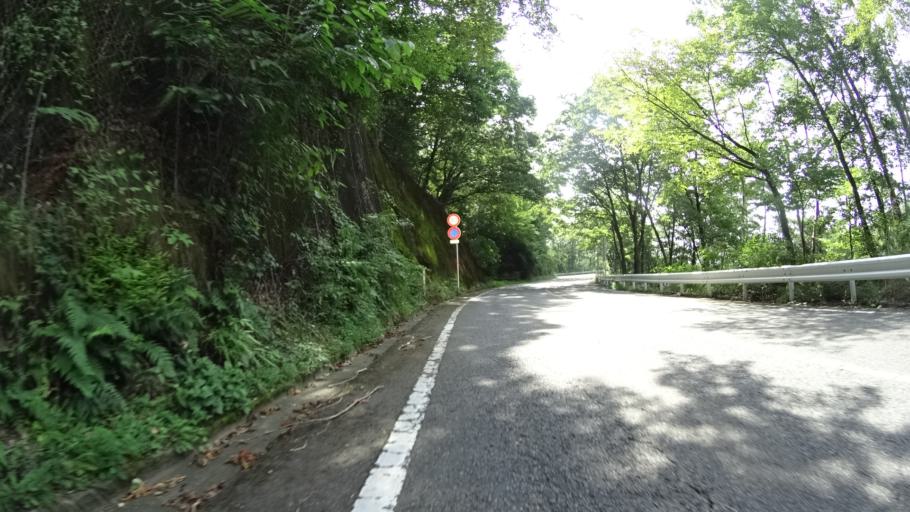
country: JP
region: Yamanashi
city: Kofu-shi
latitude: 35.7226
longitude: 138.5590
